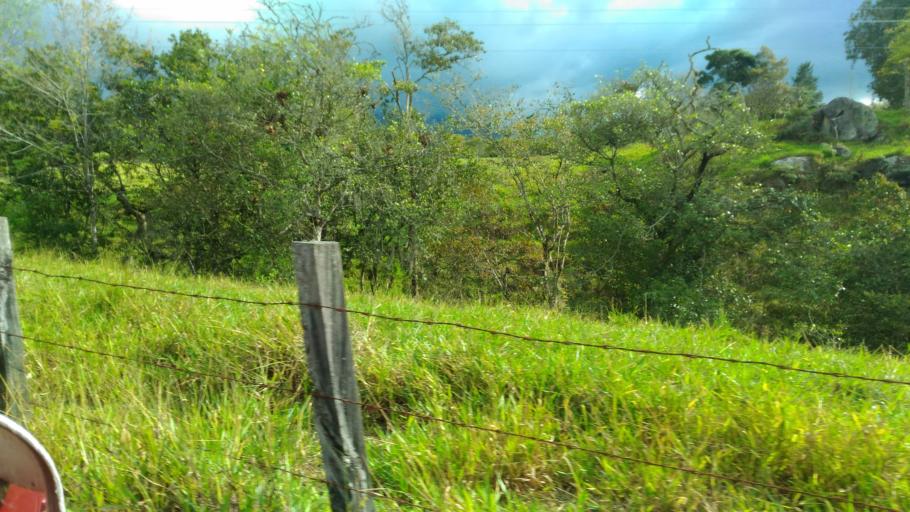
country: CO
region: Cundinamarca
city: Pacho
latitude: 5.1581
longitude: -74.1316
